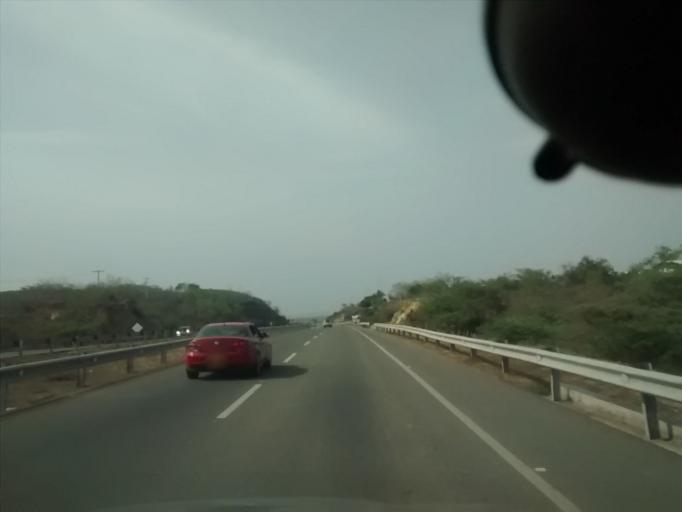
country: CO
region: Bolivar
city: Cartagena
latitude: 10.5092
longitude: -75.4716
